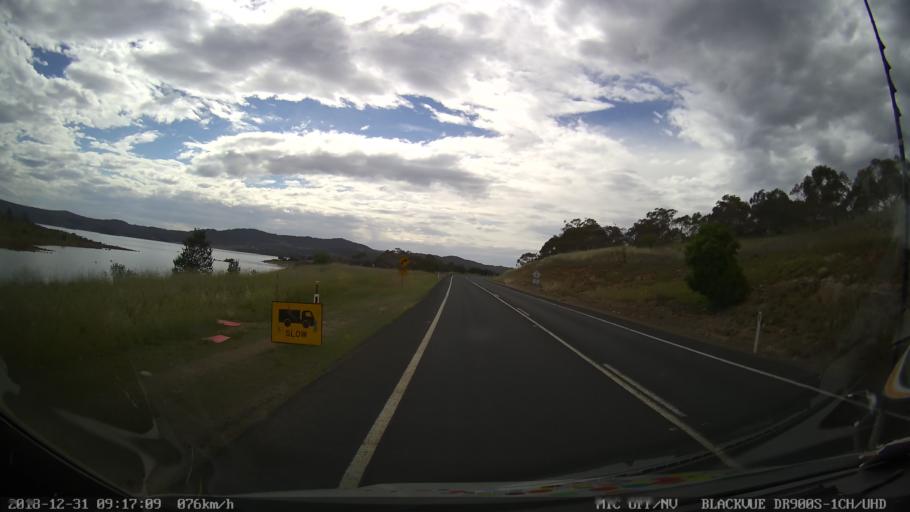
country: AU
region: New South Wales
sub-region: Snowy River
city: Jindabyne
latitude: -36.4039
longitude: 148.5978
